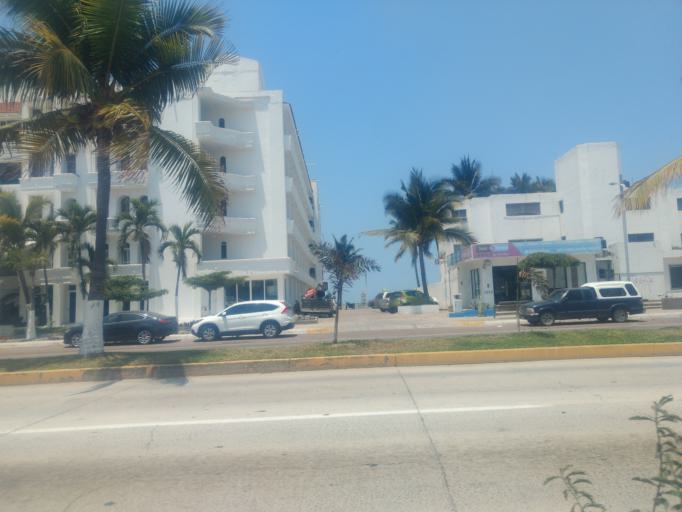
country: MX
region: Colima
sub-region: Manzanillo
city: Manzanillo
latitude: 19.0962
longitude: -104.3202
